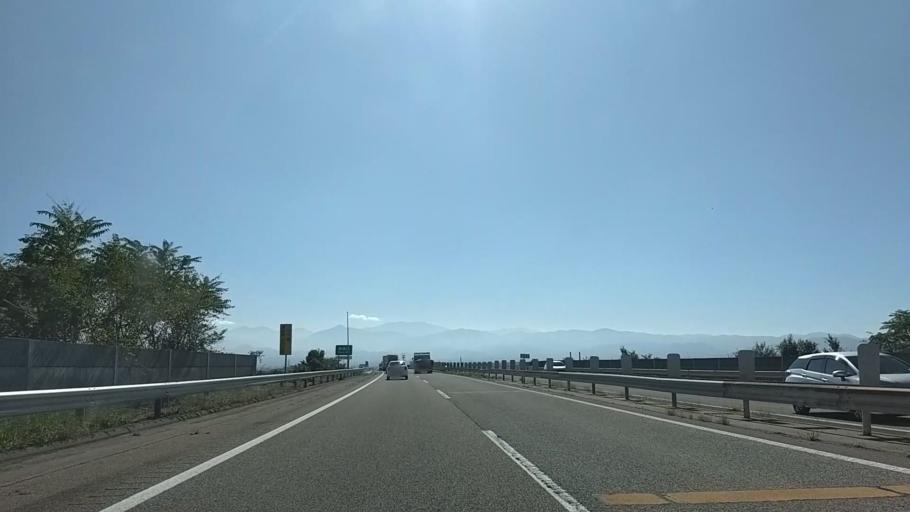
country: JP
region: Toyama
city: Toyama-shi
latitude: 36.6662
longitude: 137.1857
